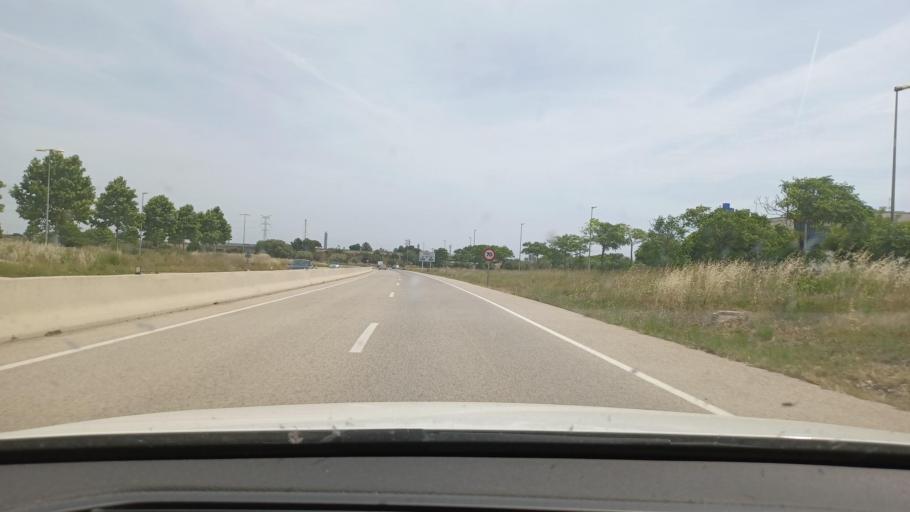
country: ES
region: Catalonia
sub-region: Provincia de Tarragona
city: Vila-seca
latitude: 41.1225
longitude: 1.1568
